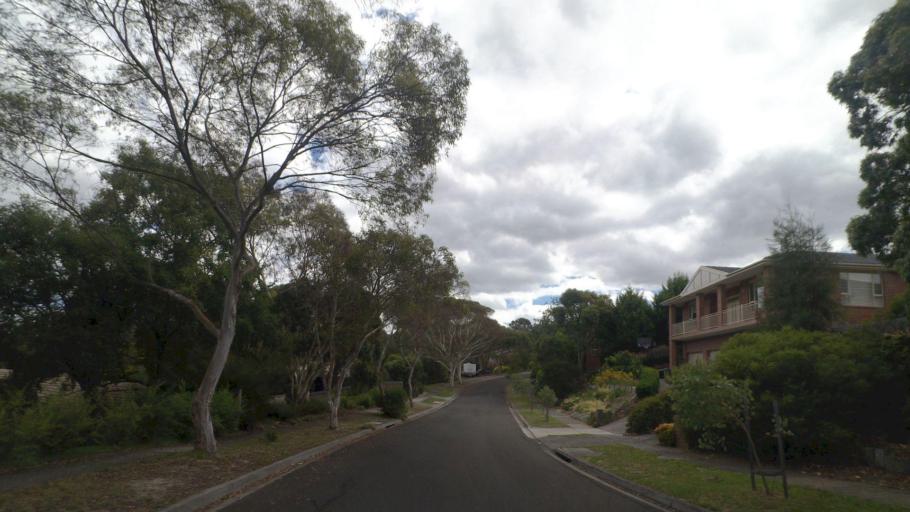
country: AU
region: Victoria
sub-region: Maroondah
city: Warranwood
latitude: -37.7763
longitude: 145.2469
